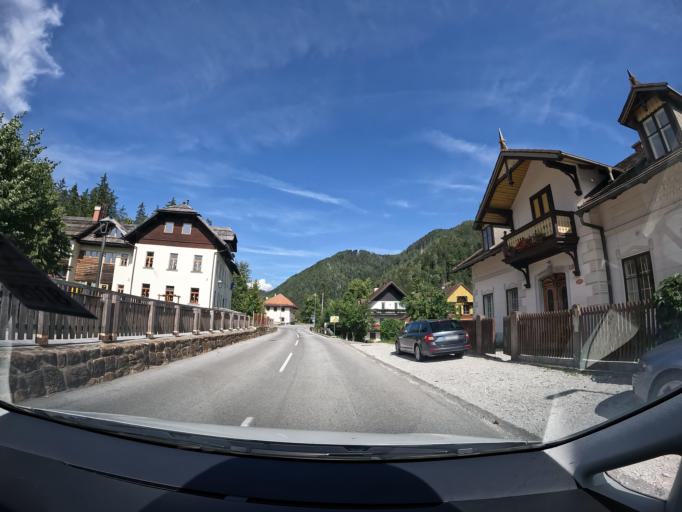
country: AT
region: Carinthia
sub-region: Politischer Bezirk Klagenfurt Land
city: Moosburg
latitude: 46.6705
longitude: 14.1253
